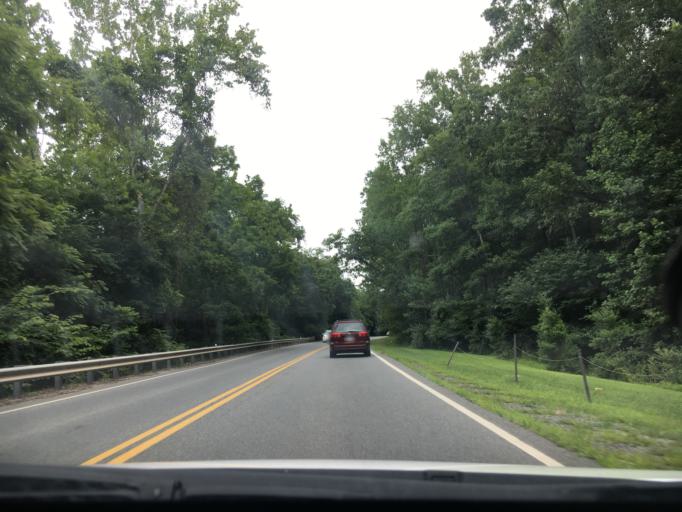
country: US
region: Virginia
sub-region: City of Charlottesville
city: Charlottesville
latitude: 38.0057
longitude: -78.4718
